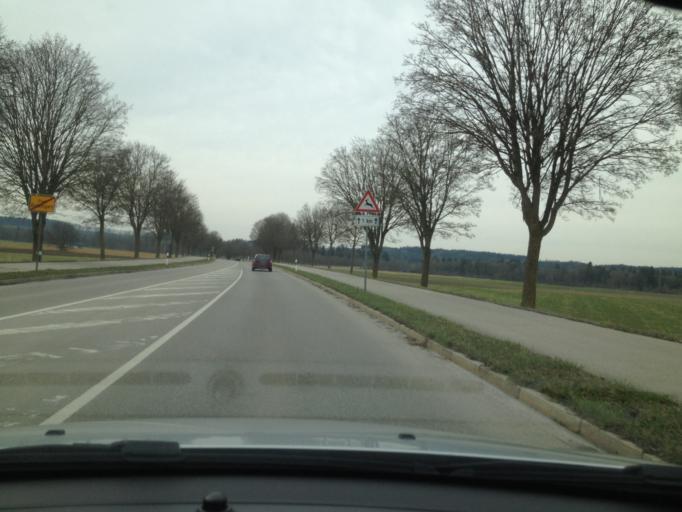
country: DE
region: Bavaria
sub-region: Swabia
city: Bobingen
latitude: 48.2706
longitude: 10.8185
